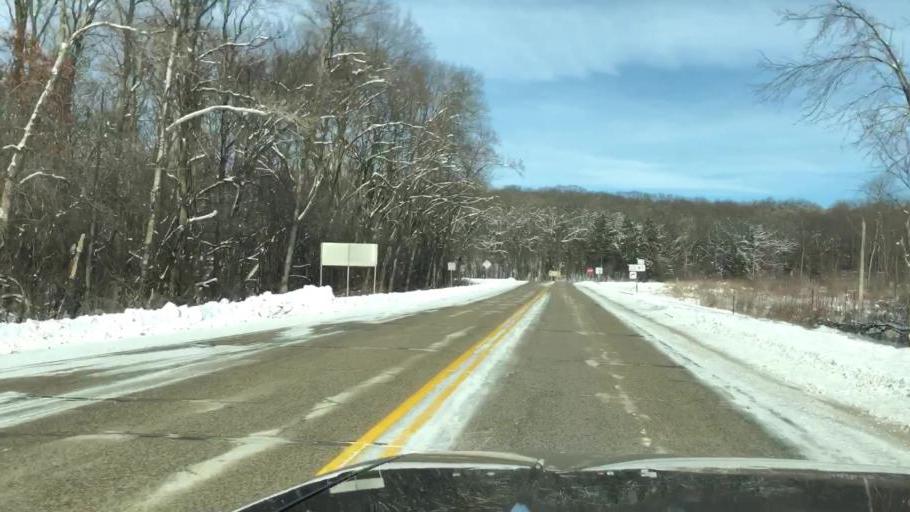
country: US
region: Wisconsin
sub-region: Waukesha County
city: Eagle
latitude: 42.9372
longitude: -88.4735
